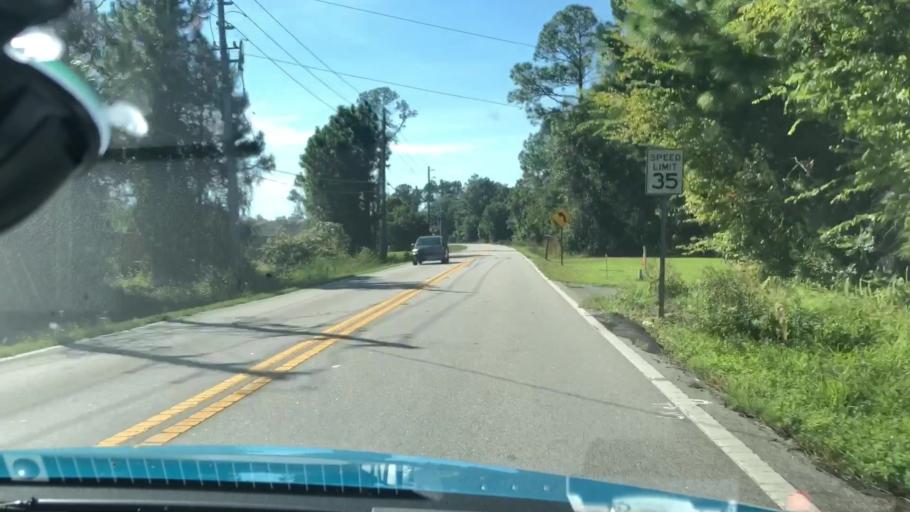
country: US
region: Florida
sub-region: Seminole County
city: Heathrow
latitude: 28.8209
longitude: -81.3609
